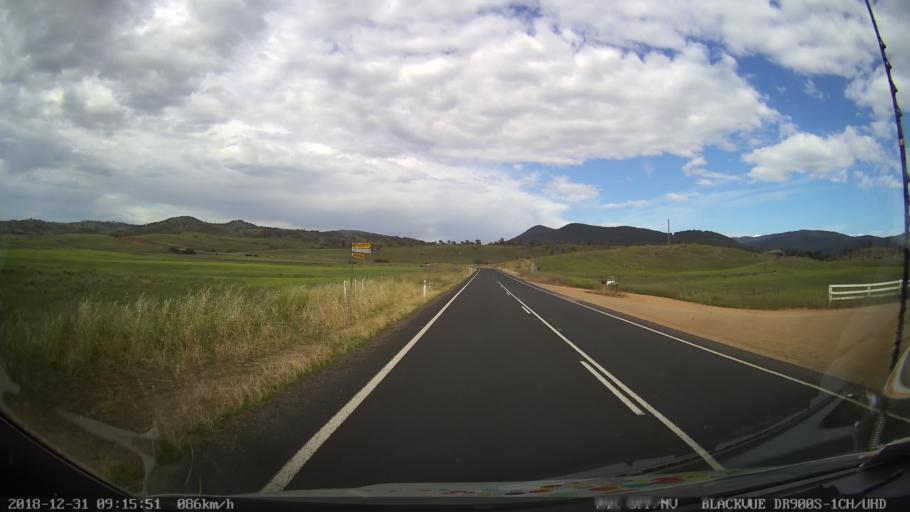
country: AU
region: New South Wales
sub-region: Snowy River
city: Jindabyne
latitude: -36.3899
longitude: 148.5972
